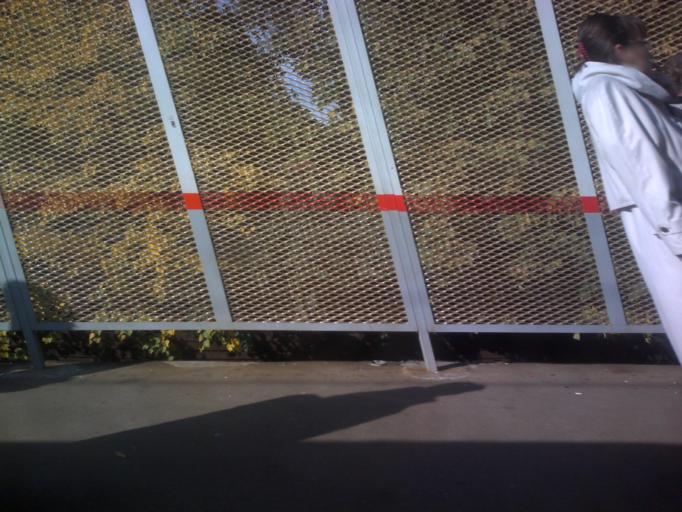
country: RU
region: Moskovskaya
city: Shcherbinka
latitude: 55.5416
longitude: 37.5705
